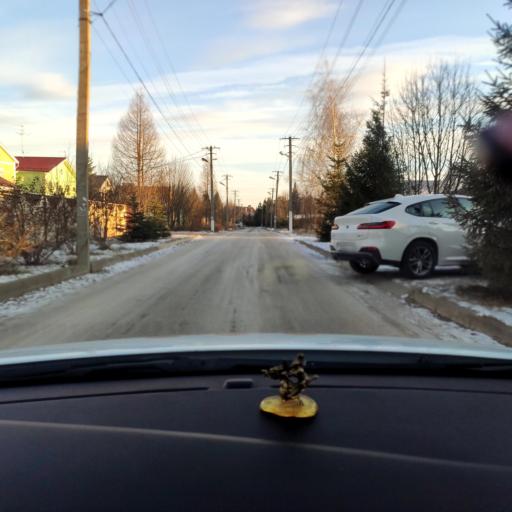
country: RU
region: Tatarstan
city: Stolbishchi
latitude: 55.6075
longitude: 49.1382
